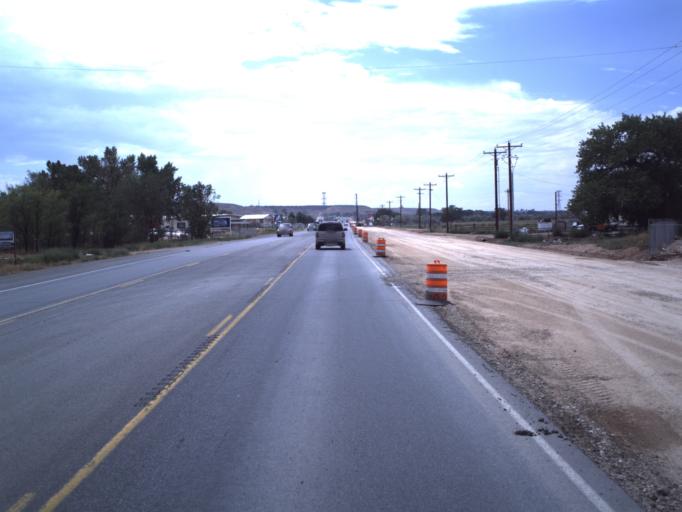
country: US
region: Utah
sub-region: Duchesne County
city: Roosevelt
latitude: 40.2696
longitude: -110.0377
